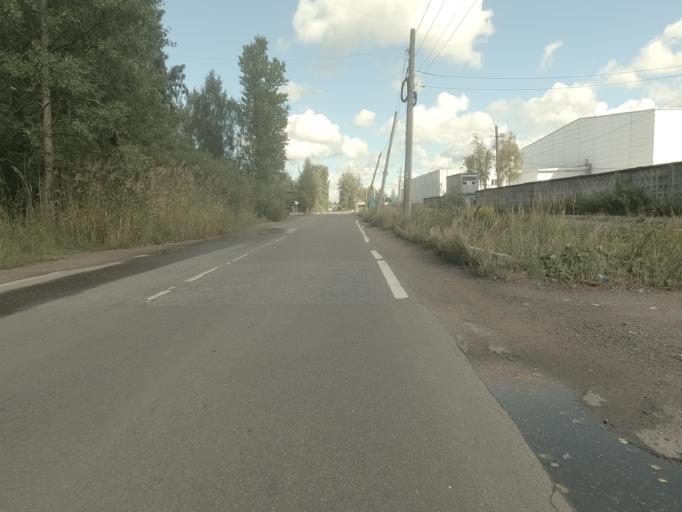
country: RU
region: Leningrad
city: Yanino Vtoroye
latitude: 59.9782
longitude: 30.5526
